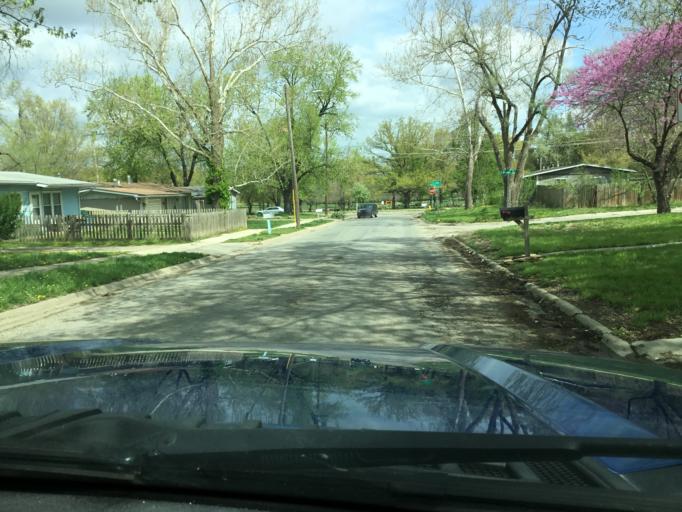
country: US
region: Kansas
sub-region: Douglas County
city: Lawrence
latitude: 38.9562
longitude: -95.2137
